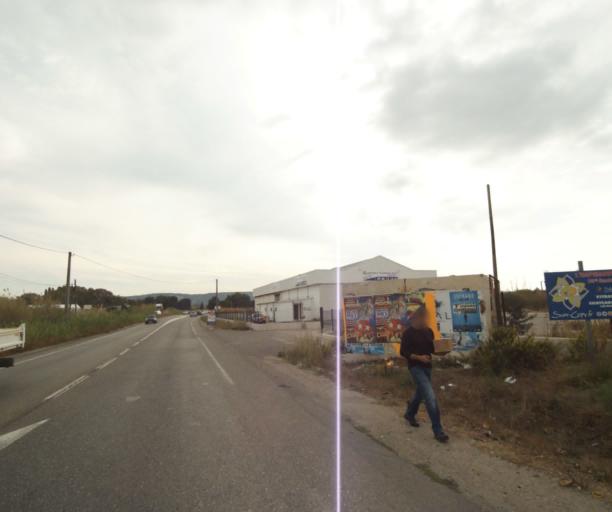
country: FR
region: Provence-Alpes-Cote d'Azur
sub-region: Departement des Bouches-du-Rhone
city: Marignane
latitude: 43.3970
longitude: 5.1980
